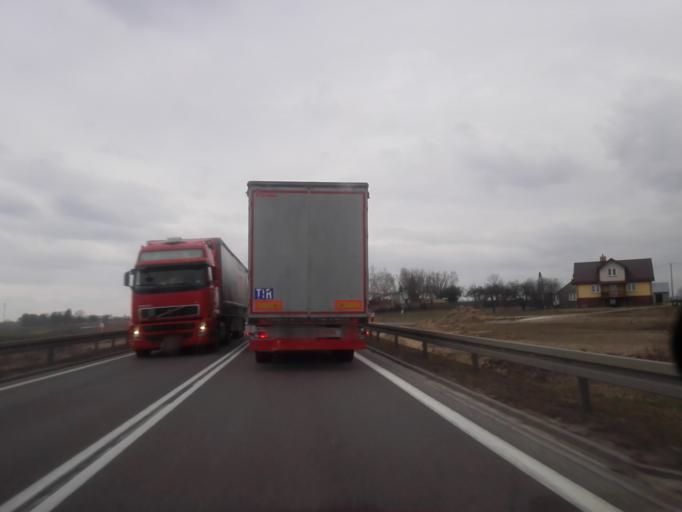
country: PL
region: Podlasie
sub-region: Powiat augustowski
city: Augustow
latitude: 53.7873
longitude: 22.8558
